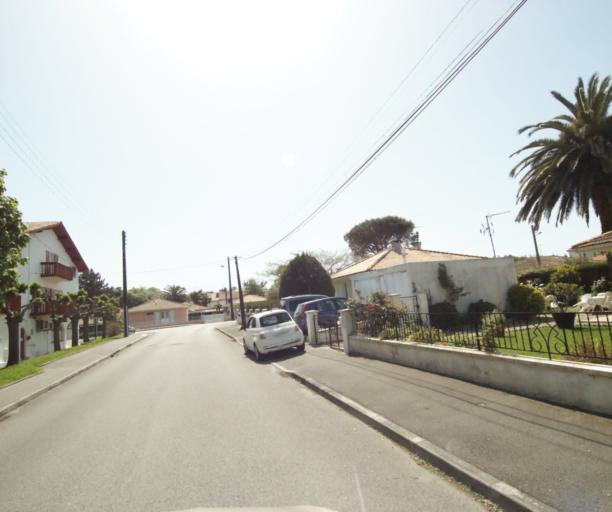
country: FR
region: Aquitaine
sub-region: Departement des Pyrenees-Atlantiques
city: Bayonne
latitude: 43.4790
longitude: -1.4598
